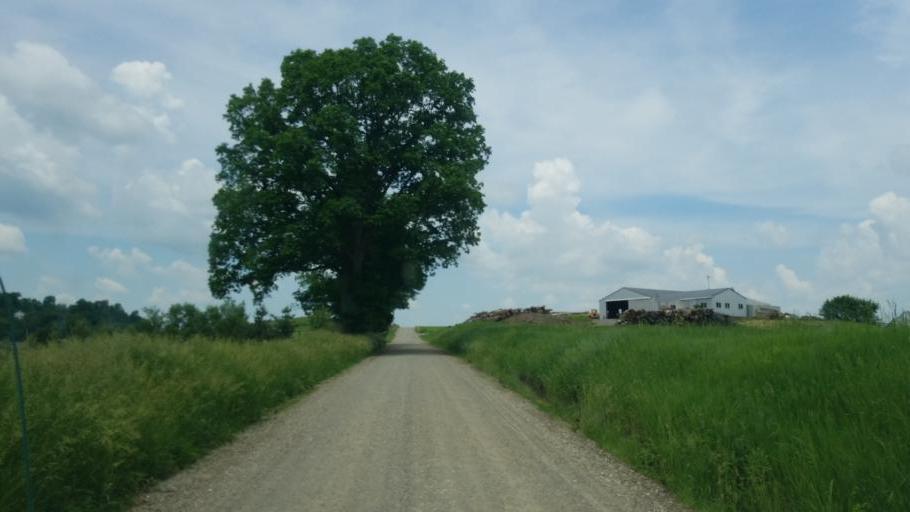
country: US
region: Ohio
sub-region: Coshocton County
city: West Lafayette
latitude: 40.4152
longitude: -81.7868
